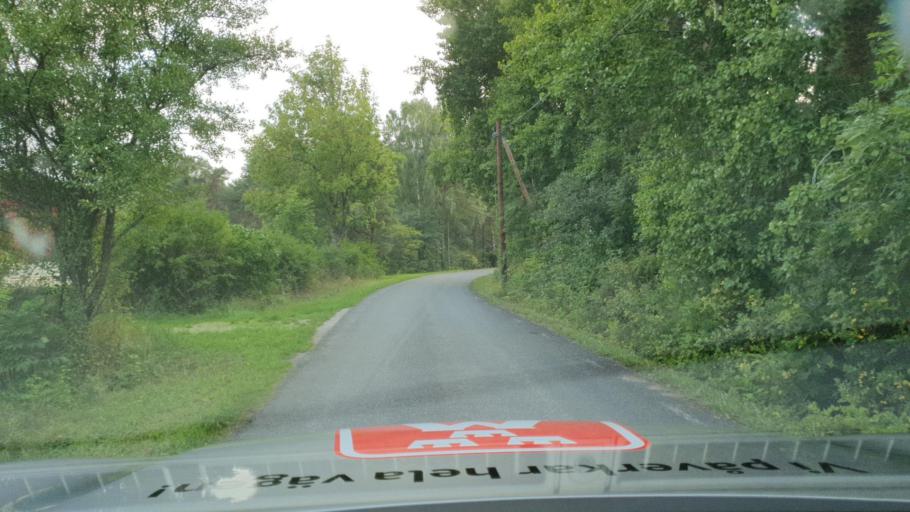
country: SE
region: Gotland
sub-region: Gotland
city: Klintehamn
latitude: 57.4495
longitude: 18.1796
